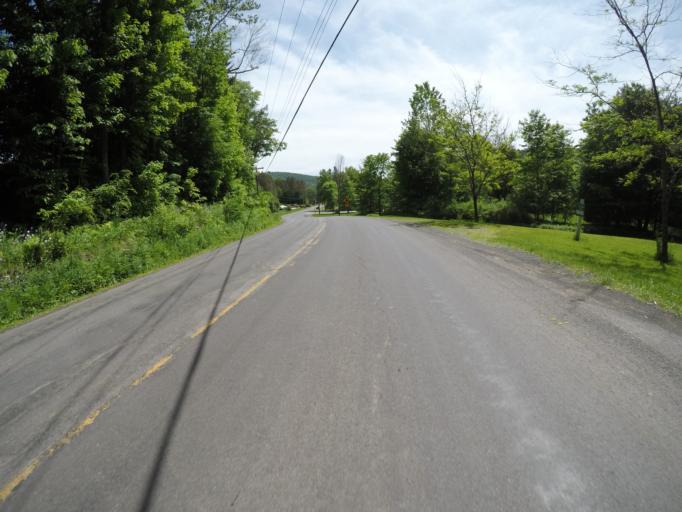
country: US
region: New York
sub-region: Delaware County
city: Delhi
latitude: 42.1844
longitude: -74.7894
